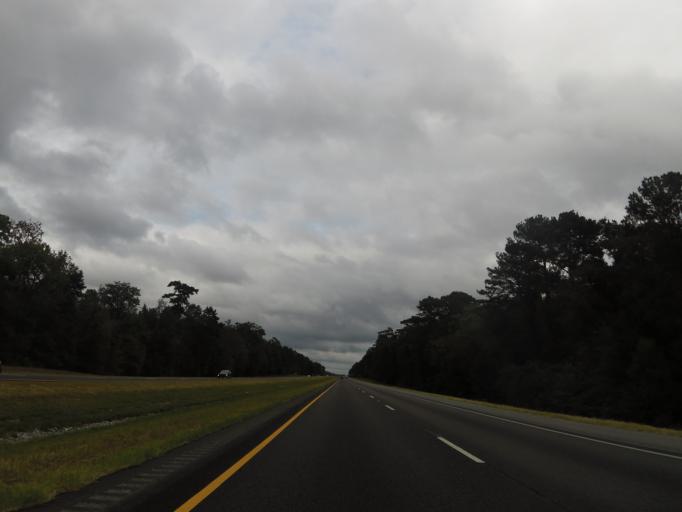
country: US
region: Alabama
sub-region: Conecuh County
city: Evergreen
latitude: 31.4057
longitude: -87.0176
